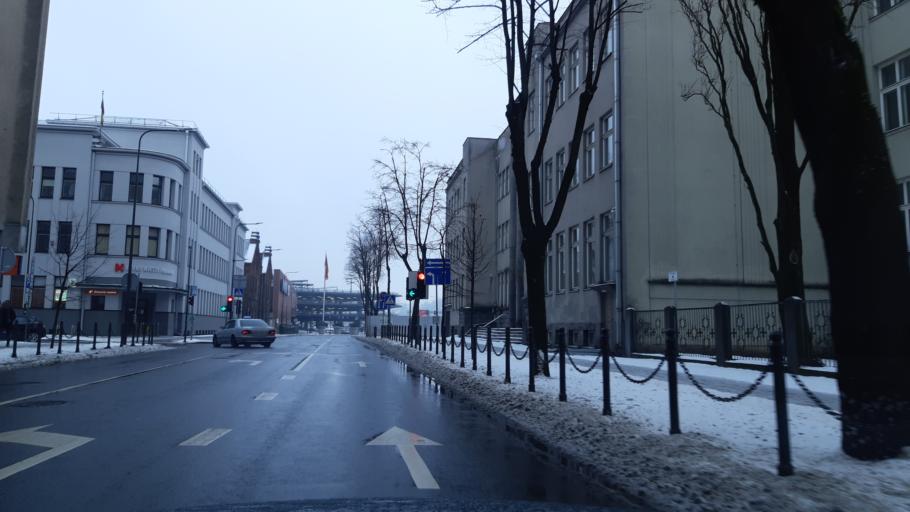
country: LT
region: Kauno apskritis
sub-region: Kaunas
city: Kaunas
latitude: 54.8943
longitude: 23.9172
